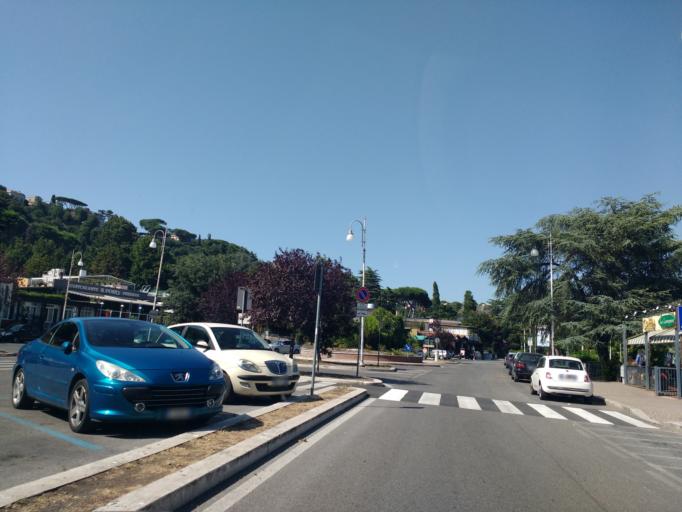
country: IT
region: Latium
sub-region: Citta metropolitana di Roma Capitale
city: Castel Gandolfo
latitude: 41.7550
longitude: 12.6509
